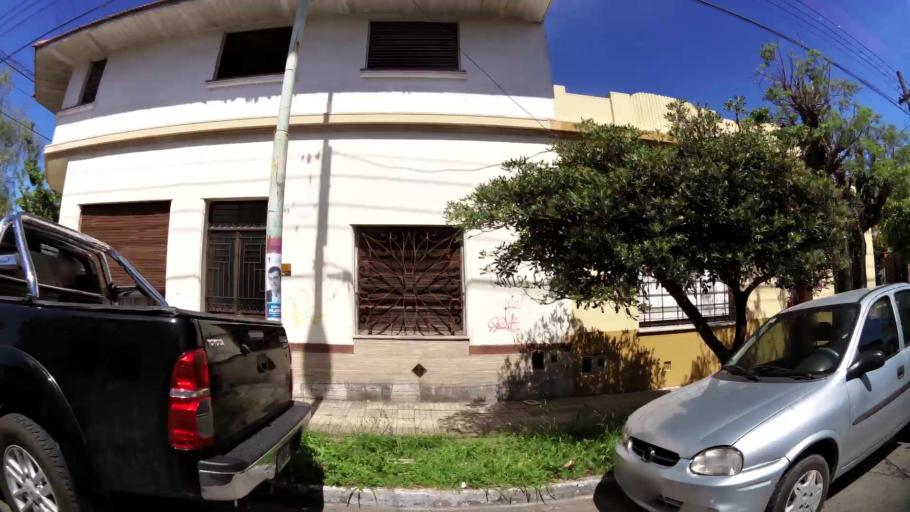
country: AR
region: Buenos Aires
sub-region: Partido de Quilmes
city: Quilmes
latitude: -34.7148
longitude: -58.2614
